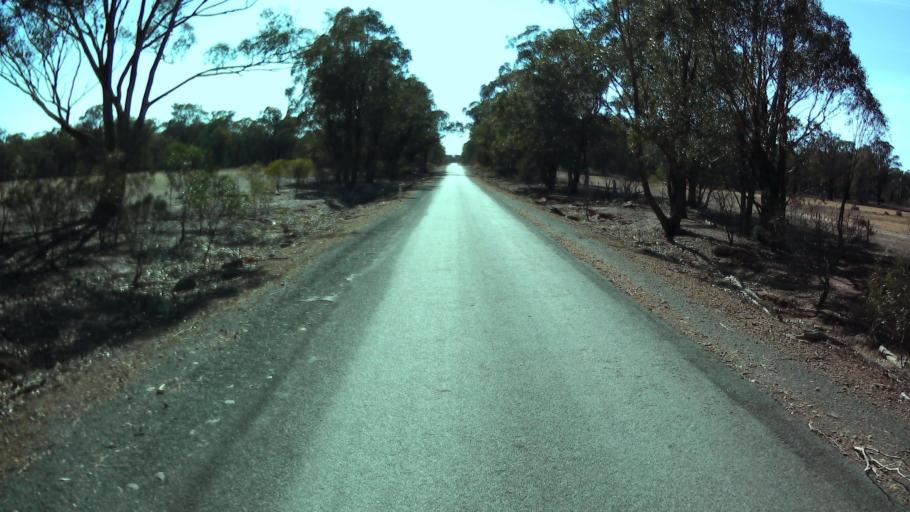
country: AU
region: New South Wales
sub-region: Weddin
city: Grenfell
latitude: -33.7844
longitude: 147.9817
